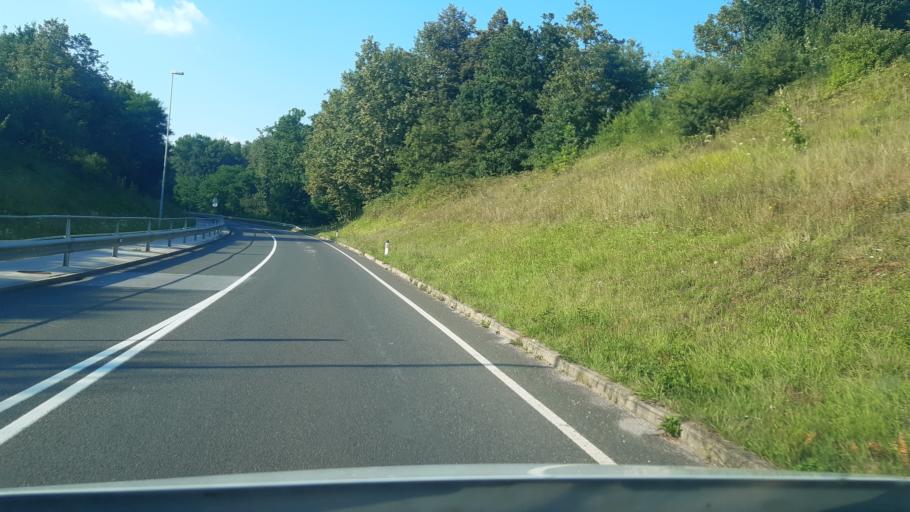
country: SI
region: Crnomelj
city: Crnomelj
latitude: 45.5780
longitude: 15.1817
